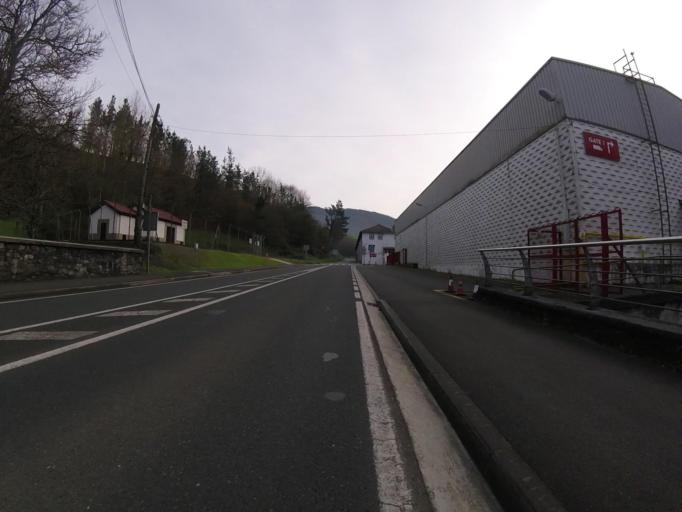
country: ES
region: Basque Country
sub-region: Provincia de Guipuzcoa
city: Berrobi
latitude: 43.1431
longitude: -2.0152
